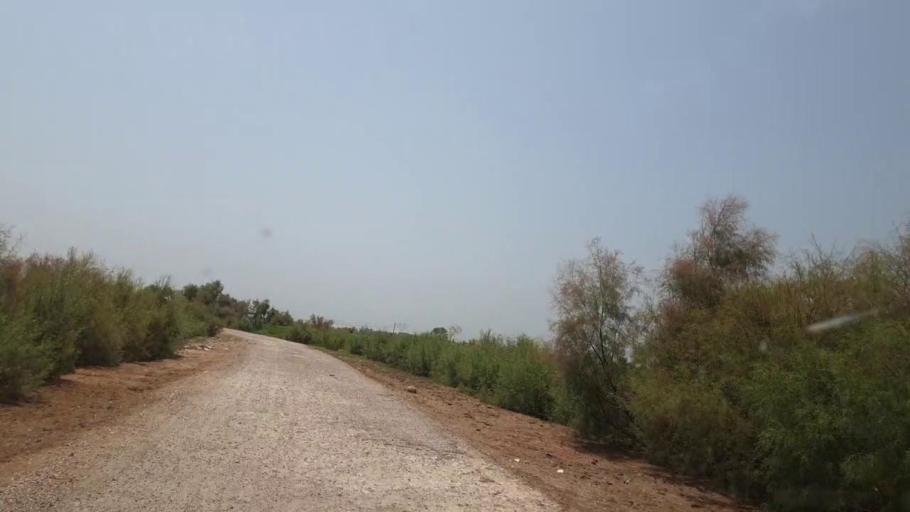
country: PK
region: Sindh
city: Shikarpur
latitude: 27.8995
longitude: 68.6318
